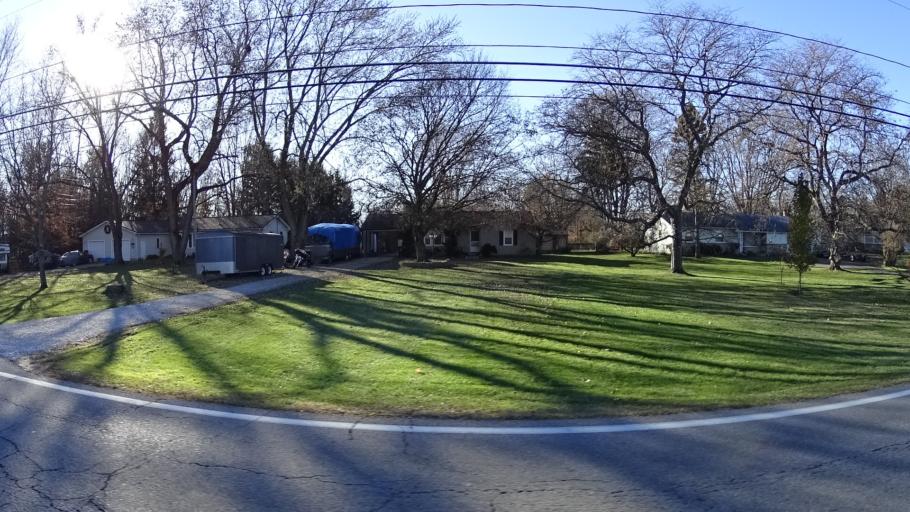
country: US
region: Ohio
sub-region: Lorain County
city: Elyria
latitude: 41.3626
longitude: -82.1445
